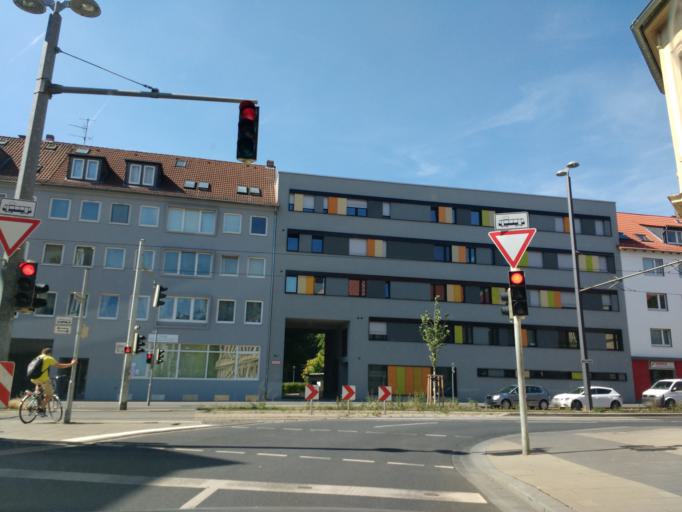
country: DE
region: Lower Saxony
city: Braunschweig
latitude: 52.2708
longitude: 10.5238
